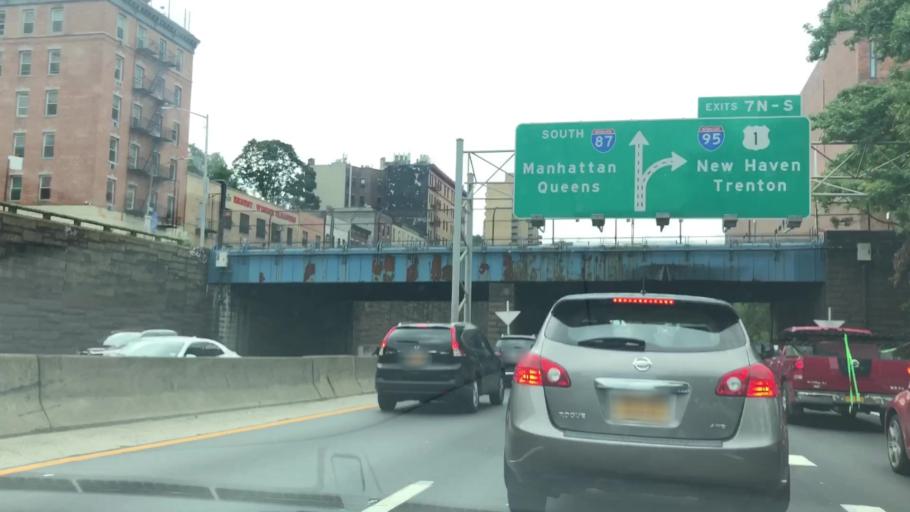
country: US
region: New York
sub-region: New York County
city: Inwood
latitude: 40.8538
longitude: -73.9196
